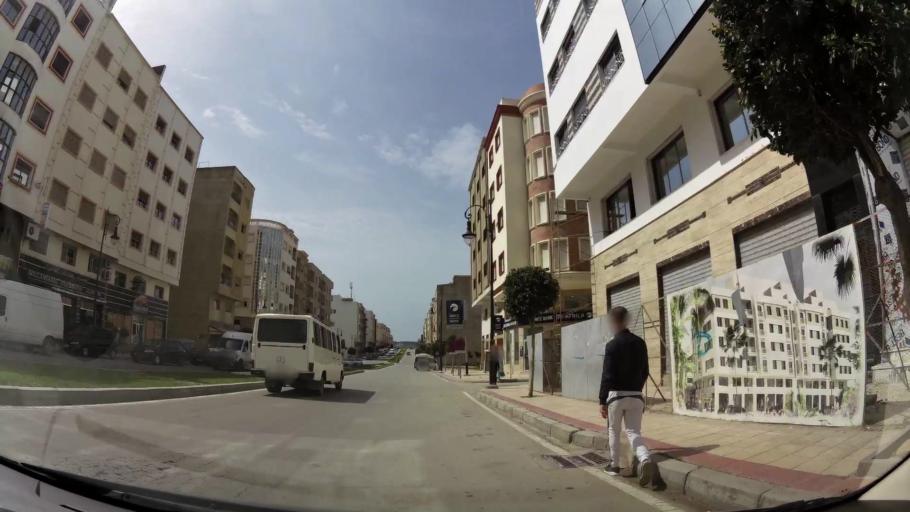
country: MA
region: Tanger-Tetouan
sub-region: Tanger-Assilah
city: Tangier
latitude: 35.7448
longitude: -5.8333
